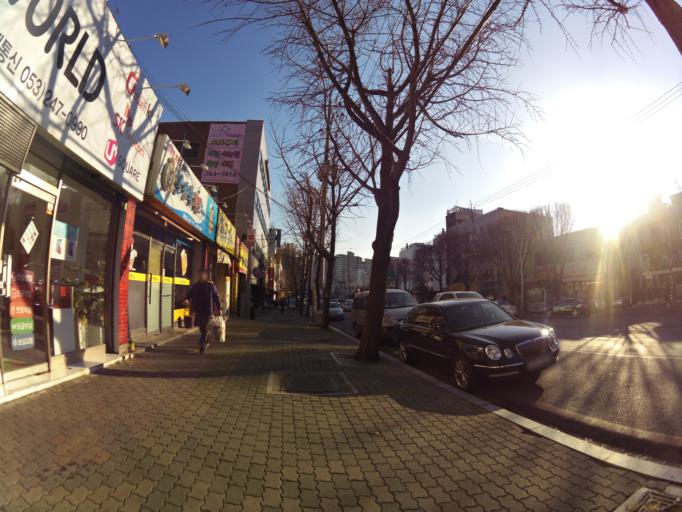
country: KR
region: Daegu
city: Daegu
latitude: 35.8746
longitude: 128.6345
